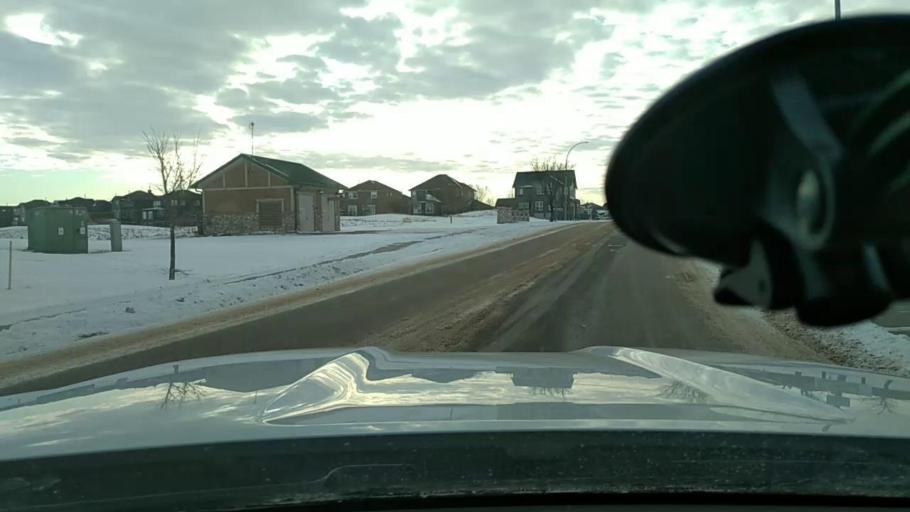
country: CA
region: Alberta
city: Chestermere
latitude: 50.9651
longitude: -113.6628
